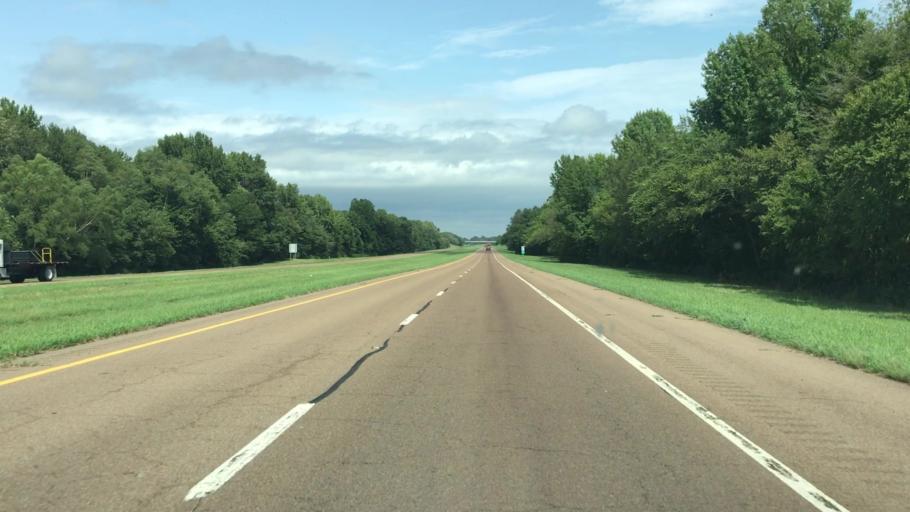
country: US
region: Tennessee
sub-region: Obion County
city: South Fulton
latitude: 36.4833
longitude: -88.9388
